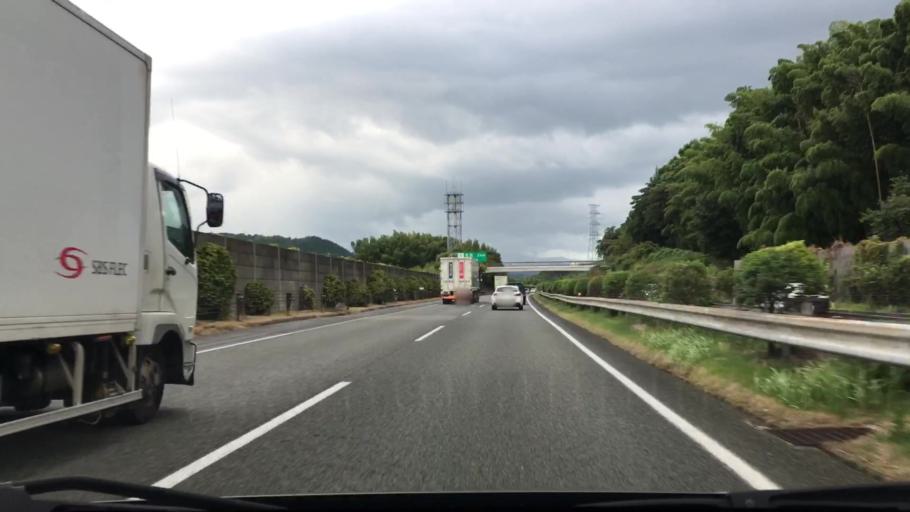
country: JP
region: Fukuoka
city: Miyata
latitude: 33.7504
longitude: 130.5842
